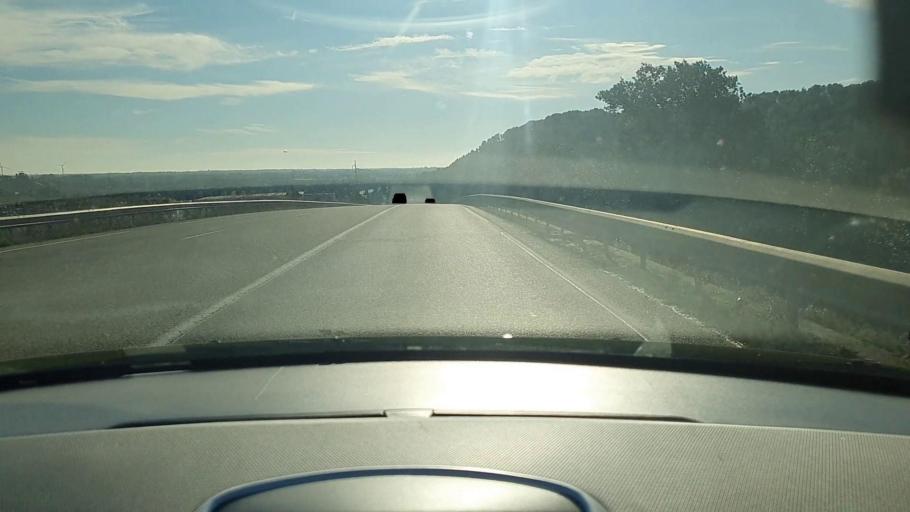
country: FR
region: Languedoc-Roussillon
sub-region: Departement du Gard
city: Beaucaire
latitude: 43.8171
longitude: 4.6107
